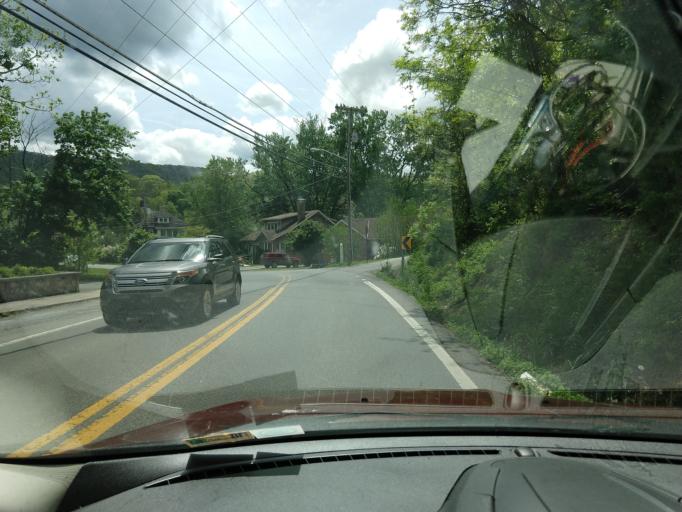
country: US
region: West Virginia
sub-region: Mercer County
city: Bluefield
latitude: 37.2526
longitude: -81.2322
